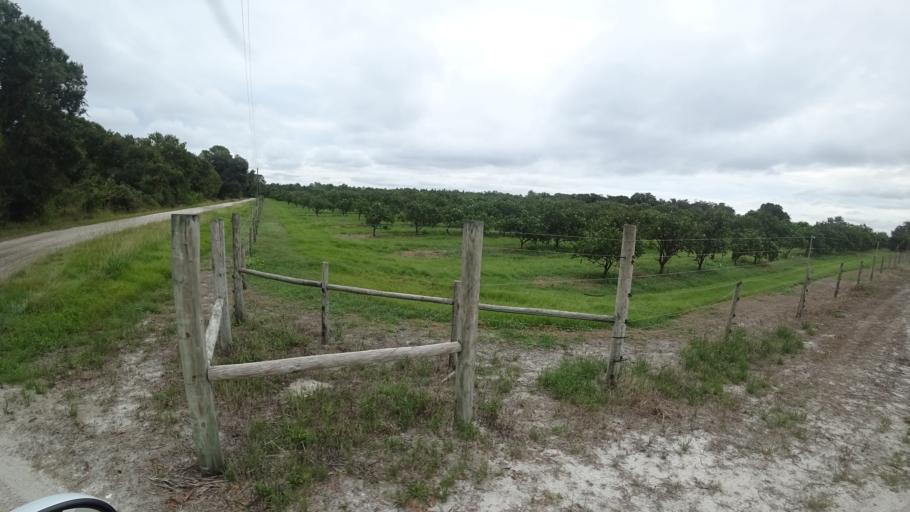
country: US
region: Florida
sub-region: Hillsborough County
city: Wimauma
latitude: 27.5728
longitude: -82.1376
